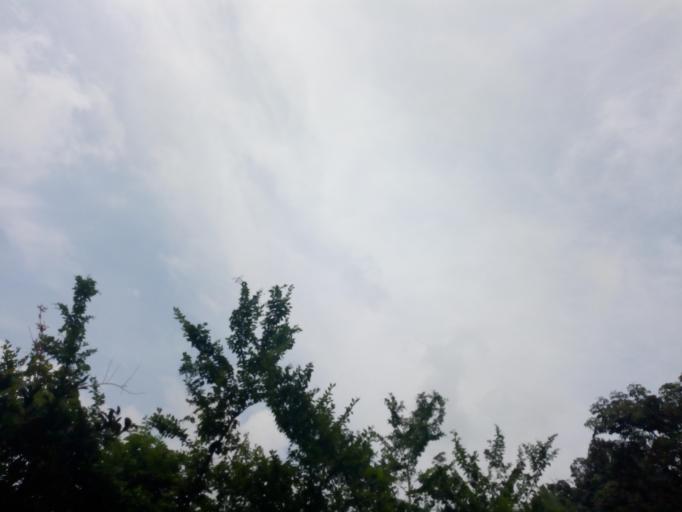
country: IN
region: Karnataka
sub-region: Dakshina Kannada
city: Sulya
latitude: 12.3808
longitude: 75.5138
